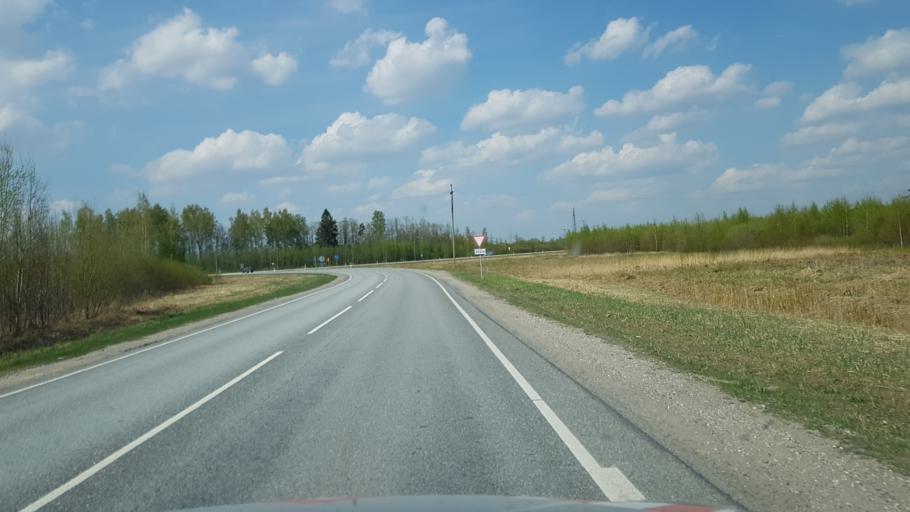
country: EE
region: Paernumaa
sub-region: Sindi linn
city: Sindi
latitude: 58.4208
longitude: 24.6700
